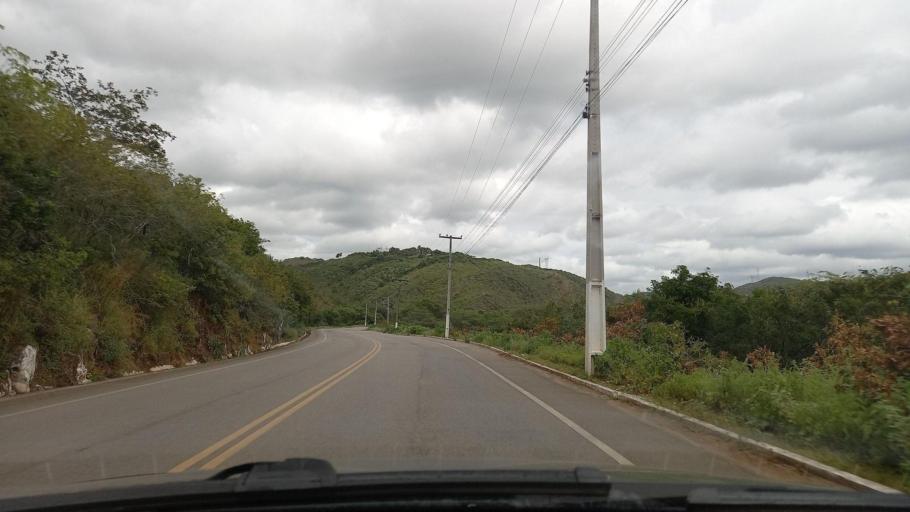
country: BR
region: Sergipe
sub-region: Caninde De Sao Francisco
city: Caninde de Sao Francisco
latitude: -9.6412
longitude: -37.7767
